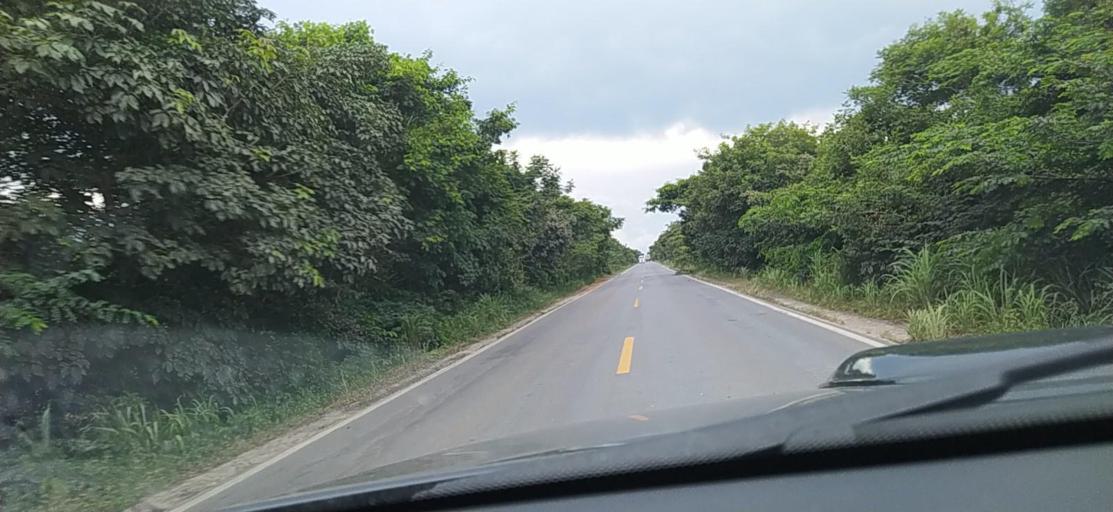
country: BR
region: Minas Gerais
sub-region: Francisco Sa
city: Francisco Sa
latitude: -16.2434
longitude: -43.6252
